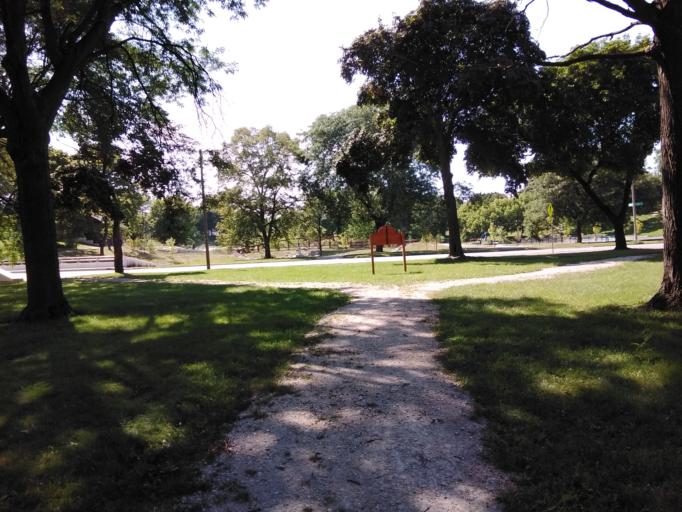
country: US
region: Wisconsin
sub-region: Milwaukee County
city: West Milwaukee
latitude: 42.9975
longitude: -87.9331
